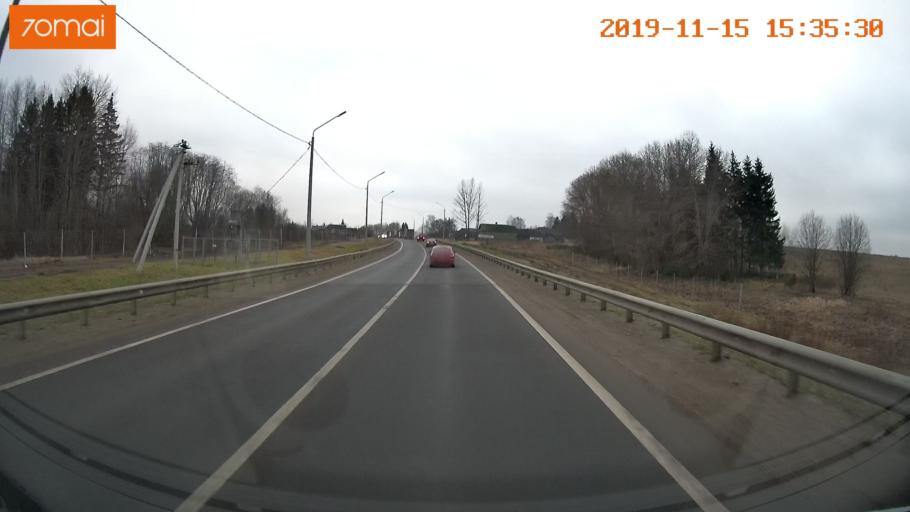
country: RU
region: Jaroslavl
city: Danilov
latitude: 58.0584
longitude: 40.0874
